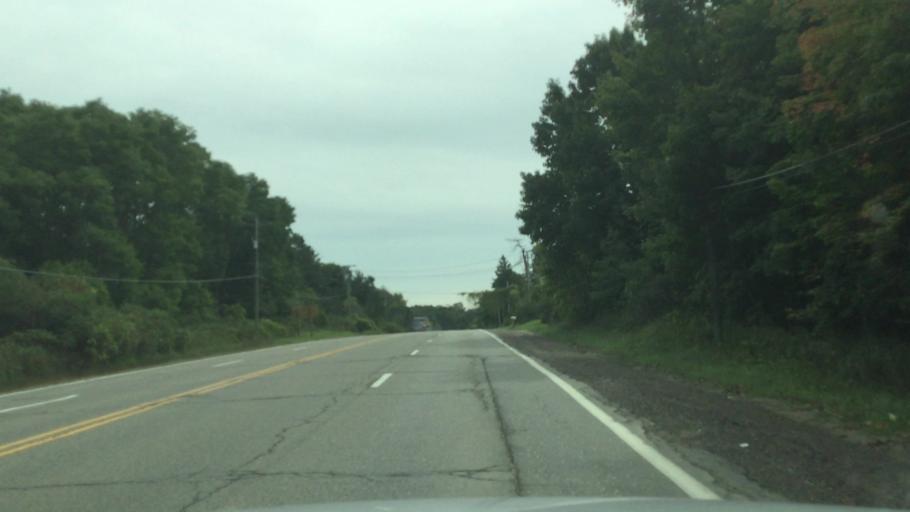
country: US
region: Michigan
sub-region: Oakland County
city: Holly
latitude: 42.8140
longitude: -83.5444
